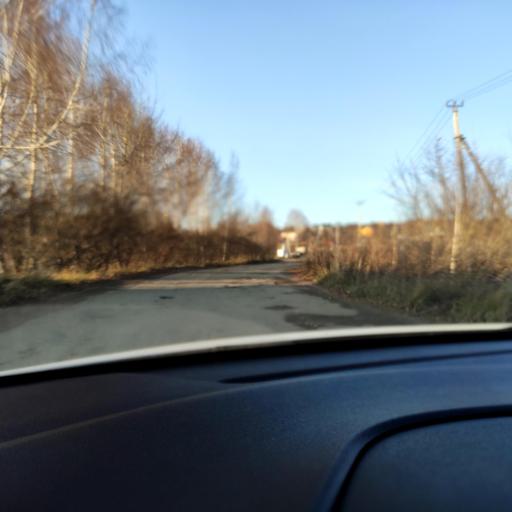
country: RU
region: Tatarstan
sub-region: Gorod Kazan'
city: Kazan
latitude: 55.8836
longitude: 49.0695
